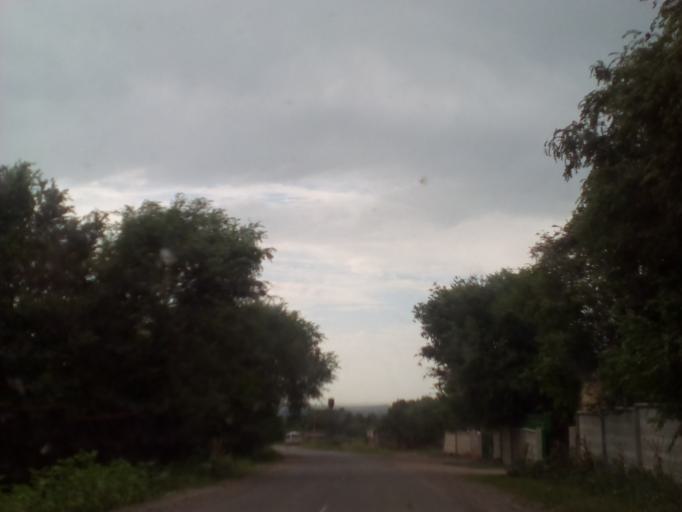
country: KZ
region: Almaty Oblysy
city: Burunday
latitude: 43.1567
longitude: 76.3844
